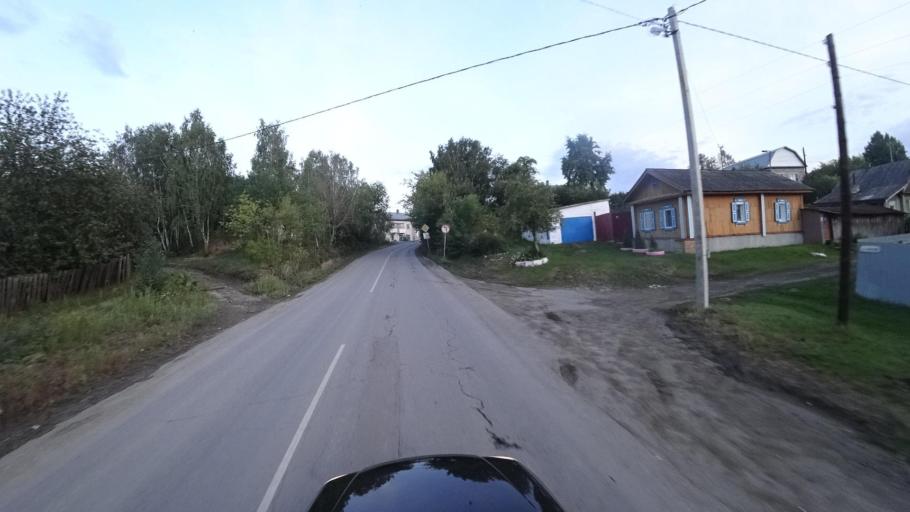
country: RU
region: Sverdlovsk
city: Kamyshlov
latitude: 56.8529
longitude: 62.7085
